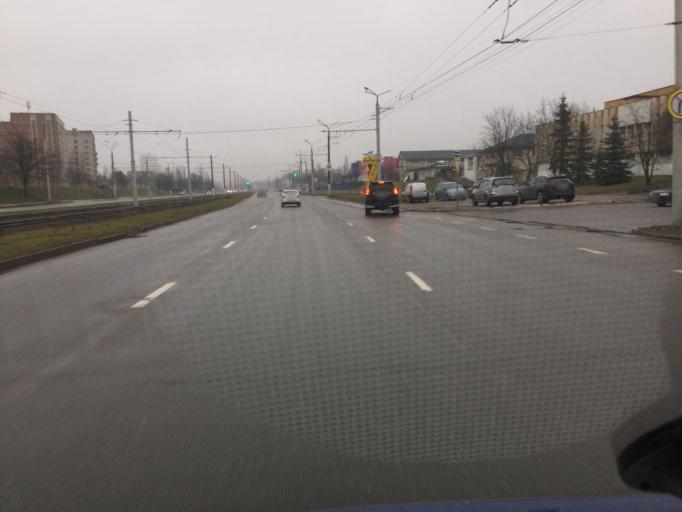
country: BY
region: Vitebsk
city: Vitebsk
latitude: 55.1588
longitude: 30.2348
